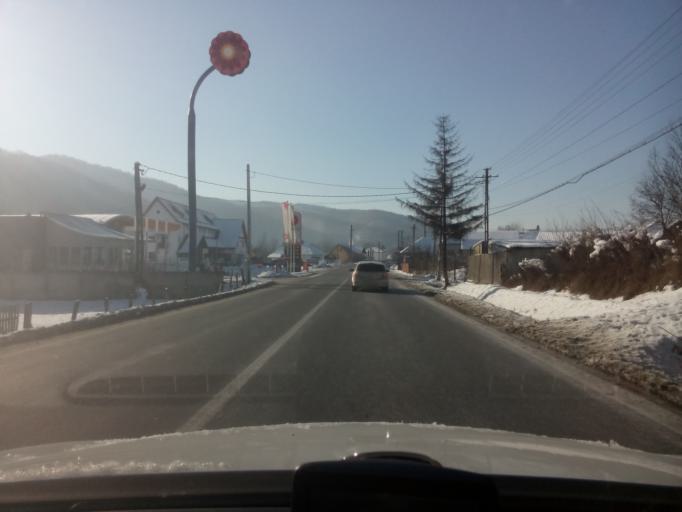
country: RO
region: Valcea
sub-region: Comuna Milcoiu
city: Milcoiu
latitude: 45.0629
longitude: 24.4329
